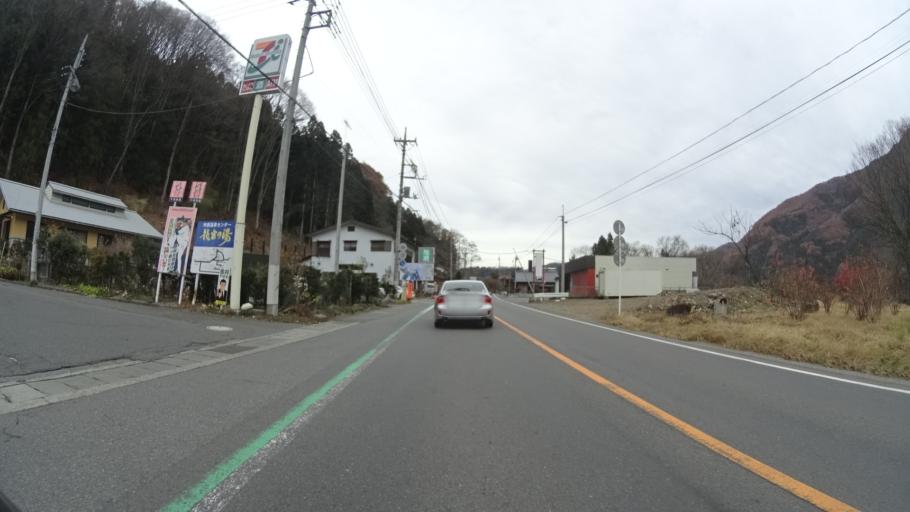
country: JP
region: Gunma
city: Numata
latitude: 36.6893
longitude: 139.2076
